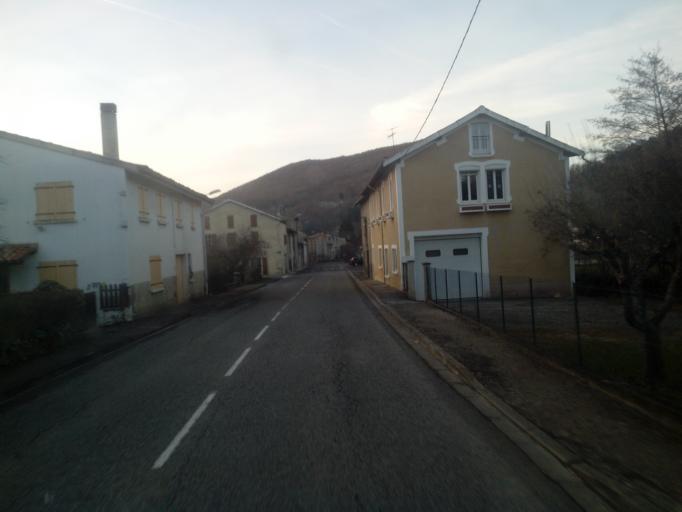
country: FR
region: Midi-Pyrenees
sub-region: Departement de l'Ariege
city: Belesta
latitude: 42.9161
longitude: 1.9036
